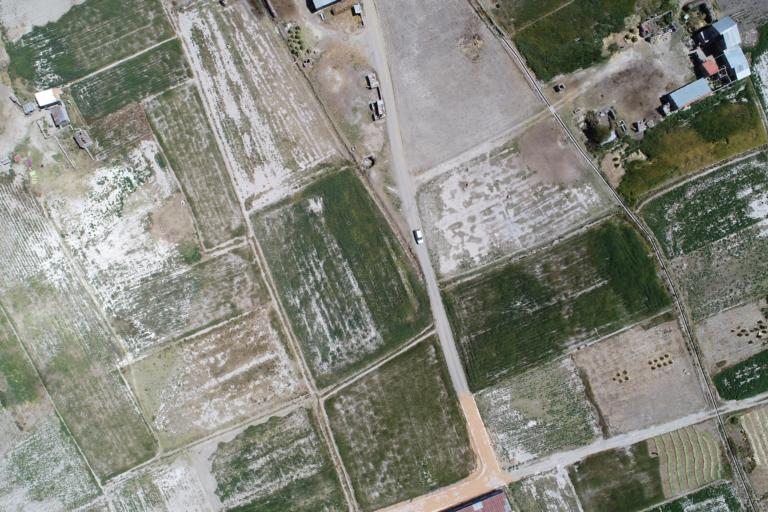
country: BO
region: La Paz
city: Achacachi
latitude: -16.0159
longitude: -68.7210
